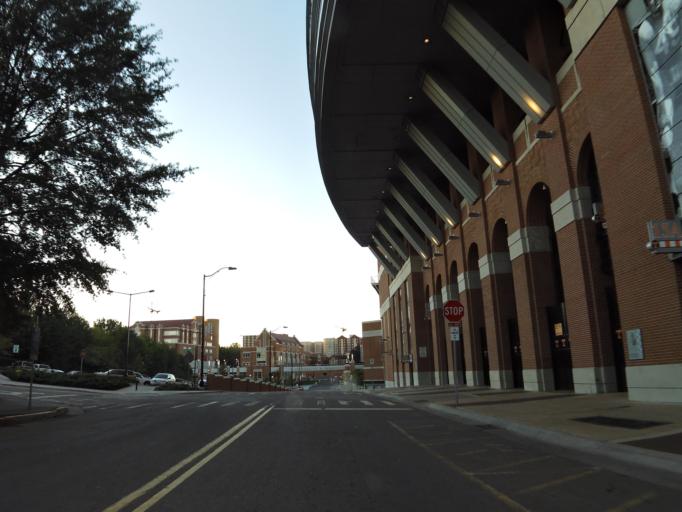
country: US
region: Tennessee
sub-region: Knox County
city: Knoxville
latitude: 35.9542
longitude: -83.9258
